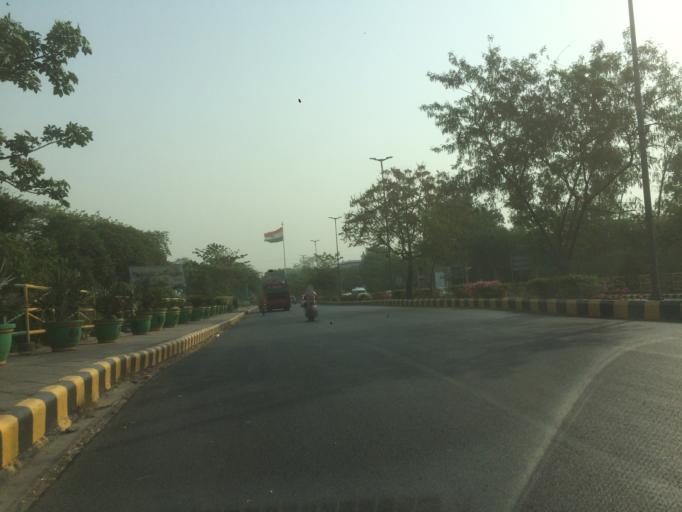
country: IN
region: NCT
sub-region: New Delhi
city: New Delhi
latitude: 28.5836
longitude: 77.1834
